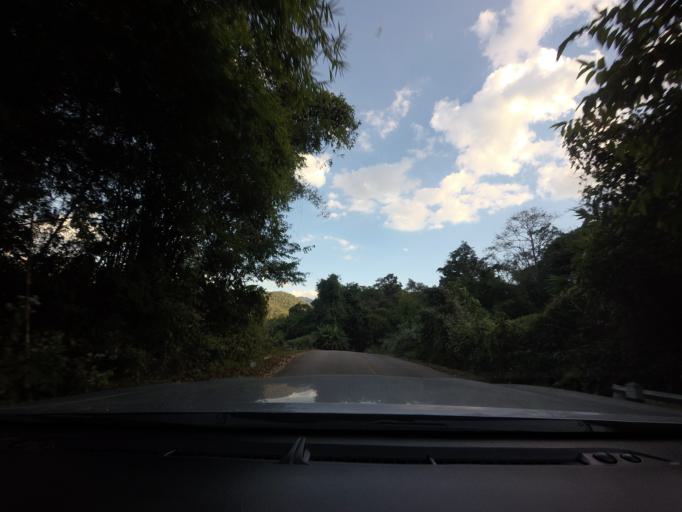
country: TH
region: Chiang Mai
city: Phrao
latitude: 19.5366
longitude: 99.1594
